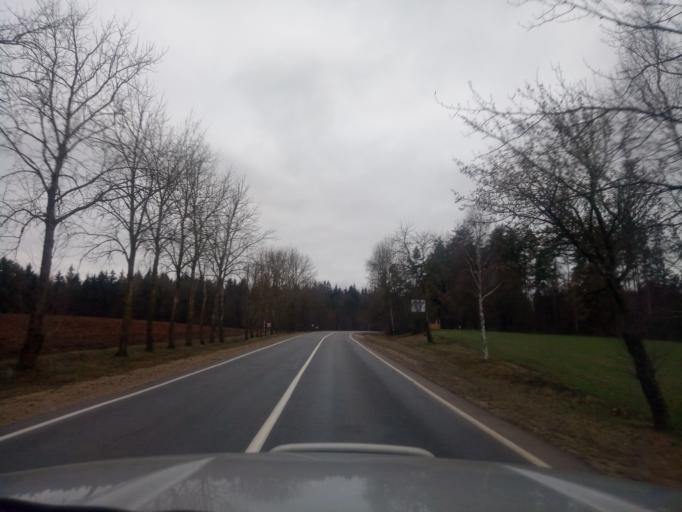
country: BY
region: Minsk
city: Kapyl'
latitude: 53.1652
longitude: 27.1217
